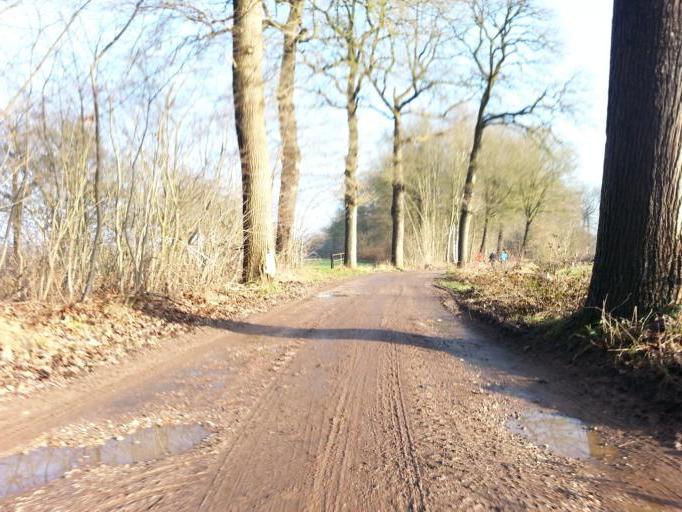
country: NL
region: Utrecht
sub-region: Gemeente Woudenberg
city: Woudenberg
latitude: 52.0943
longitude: 5.4018
